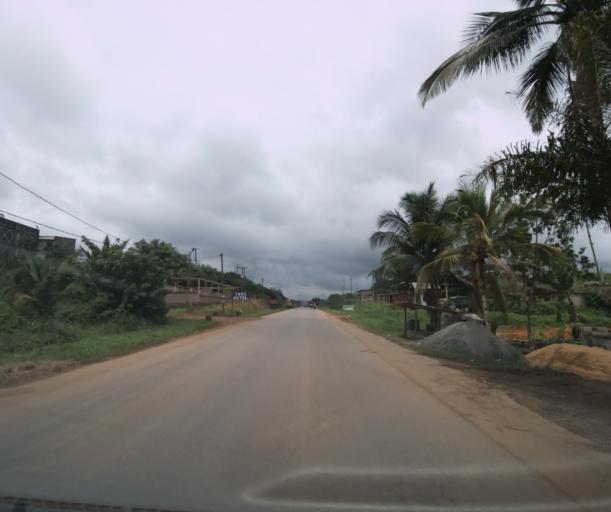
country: CM
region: Littoral
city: Edea
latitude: 3.7864
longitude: 10.1393
